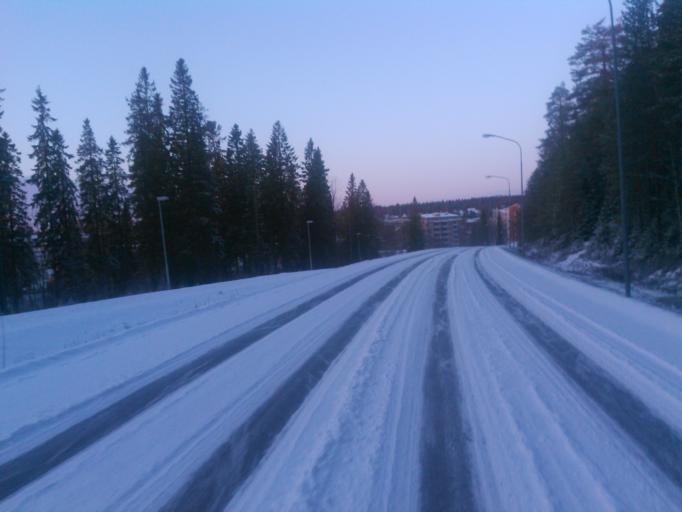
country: SE
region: Vaesterbotten
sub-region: Umea Kommun
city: Umea
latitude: 63.8233
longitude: 20.3143
